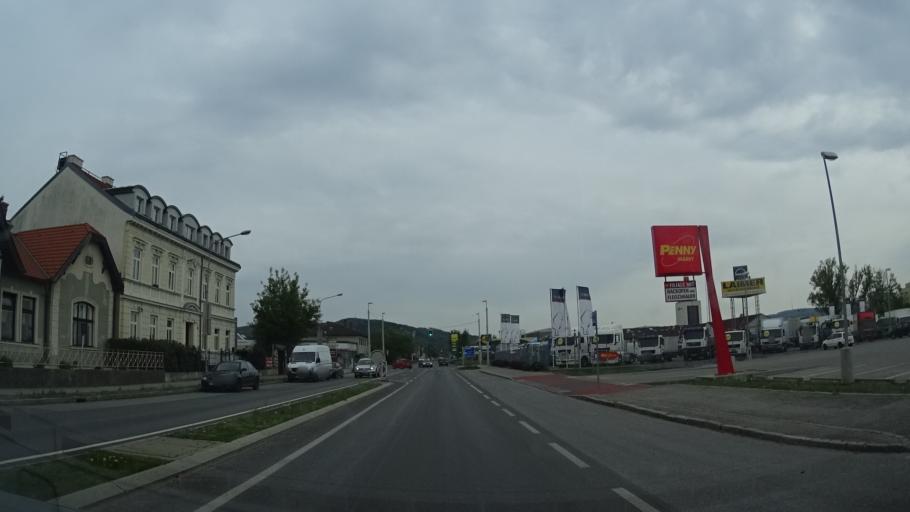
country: AT
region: Lower Austria
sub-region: Politischer Bezirk Korneuburg
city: Korneuburg
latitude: 48.3393
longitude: 16.3379
